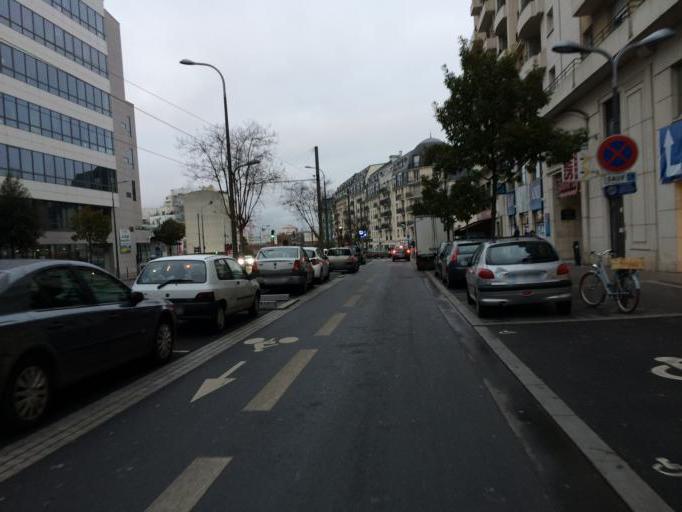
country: FR
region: Ile-de-France
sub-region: Departement des Hauts-de-Seine
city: Chatillon
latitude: 48.8090
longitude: 2.2973
